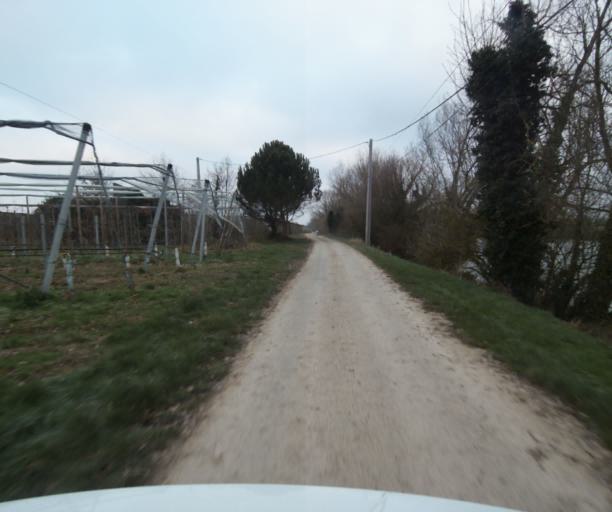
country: FR
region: Midi-Pyrenees
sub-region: Departement du Tarn-et-Garonne
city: Moissac
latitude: 44.0929
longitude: 1.1184
